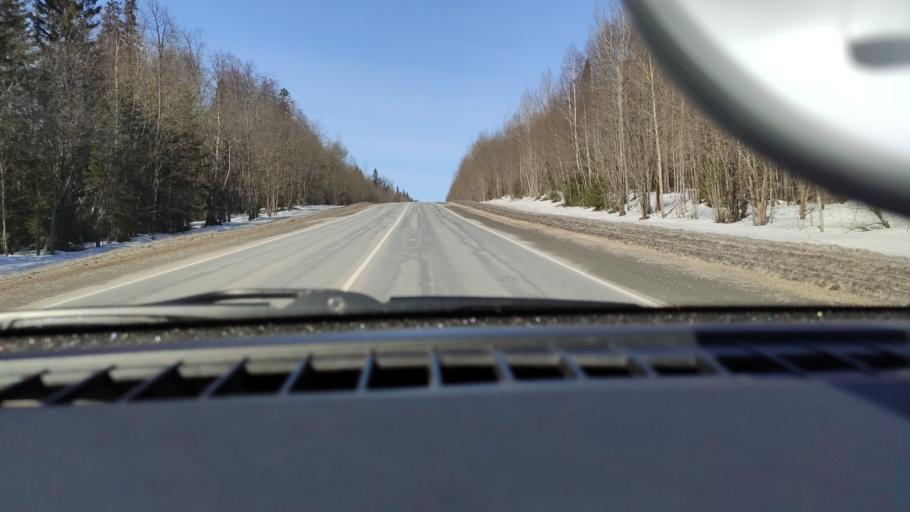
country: RU
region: Perm
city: Perm
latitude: 58.1671
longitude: 56.2387
